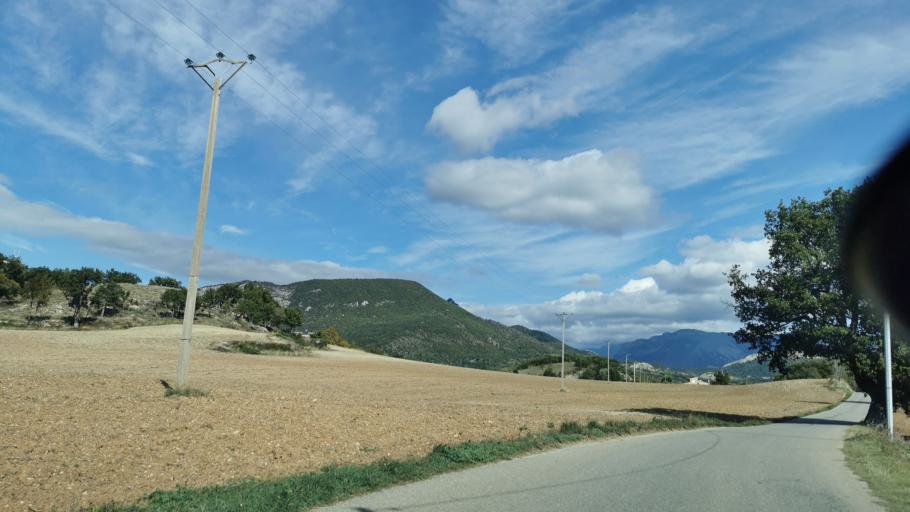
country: FR
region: Provence-Alpes-Cote d'Azur
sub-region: Departement des Alpes-de-Haute-Provence
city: Sisteron
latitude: 44.1791
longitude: 5.9772
